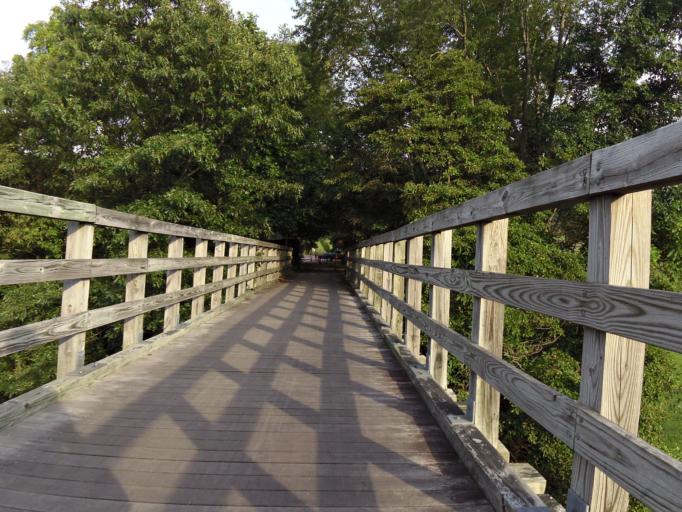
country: US
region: Virginia
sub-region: Washington County
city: Abingdon
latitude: 36.6784
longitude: -81.9360
